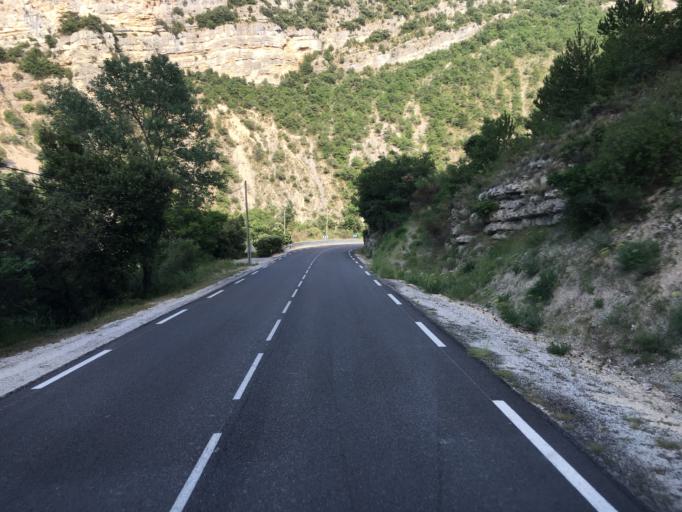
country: FR
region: Rhone-Alpes
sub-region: Departement de la Drome
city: Buis-les-Baronnies
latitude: 44.4284
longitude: 5.2783
